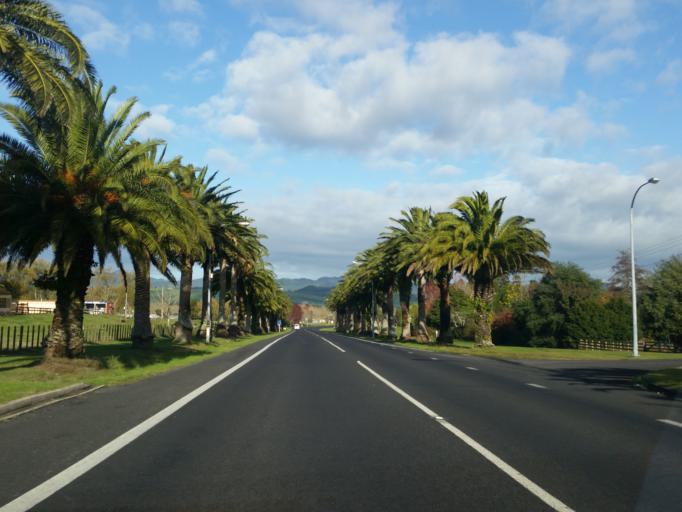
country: NZ
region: Waikato
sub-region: Hauraki District
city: Waihi
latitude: -37.3976
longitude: 175.8271
